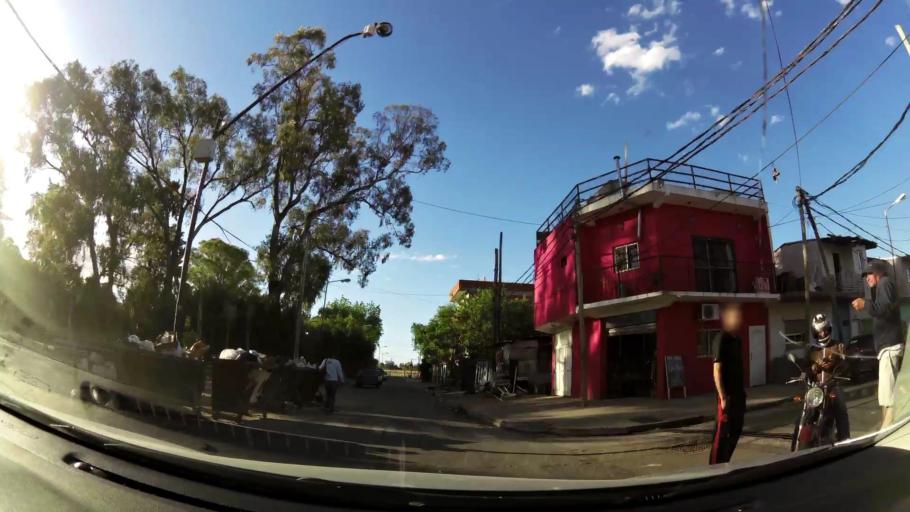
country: AR
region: Buenos Aires
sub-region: Partido de Tigre
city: Tigre
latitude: -34.4605
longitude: -58.5531
